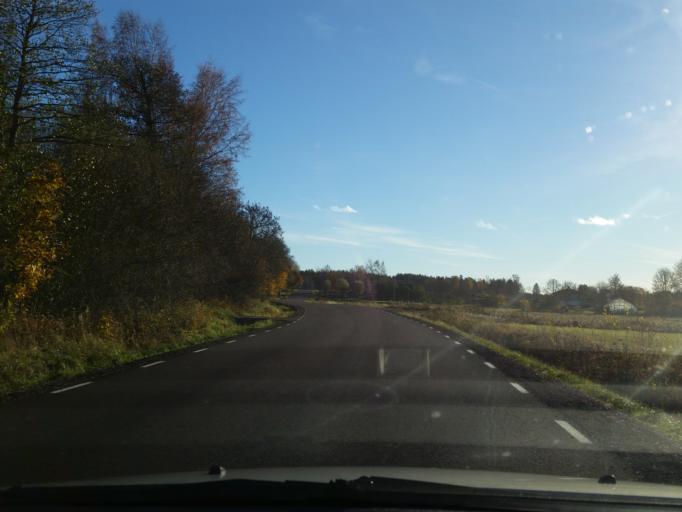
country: AX
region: Alands landsbygd
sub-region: Jomala
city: Jomala
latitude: 60.1885
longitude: 19.9608
